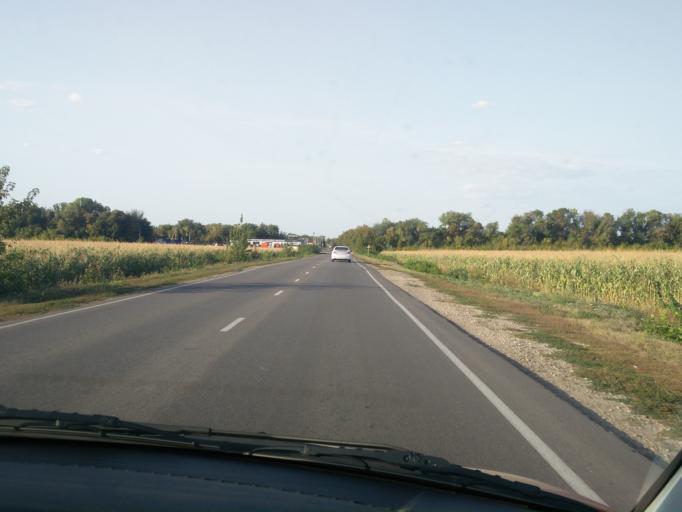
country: RU
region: Voronezj
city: Ramon'
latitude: 51.9148
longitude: 39.3193
